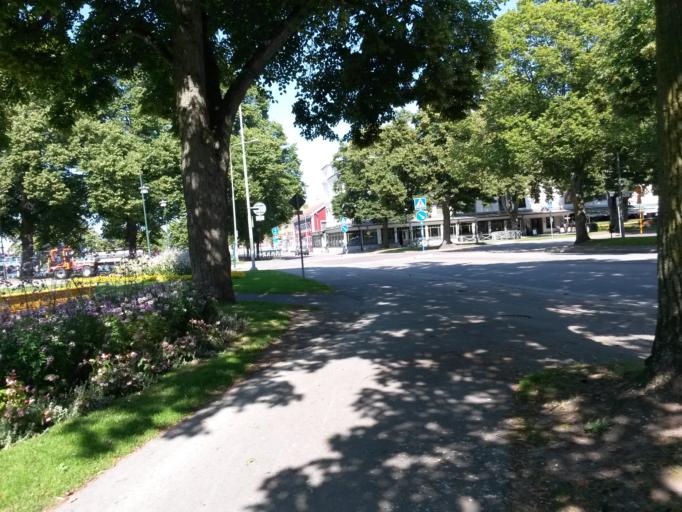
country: SE
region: Vaestra Goetaland
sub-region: Lidkopings Kommun
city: Lidkoping
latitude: 58.5028
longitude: 13.1603
